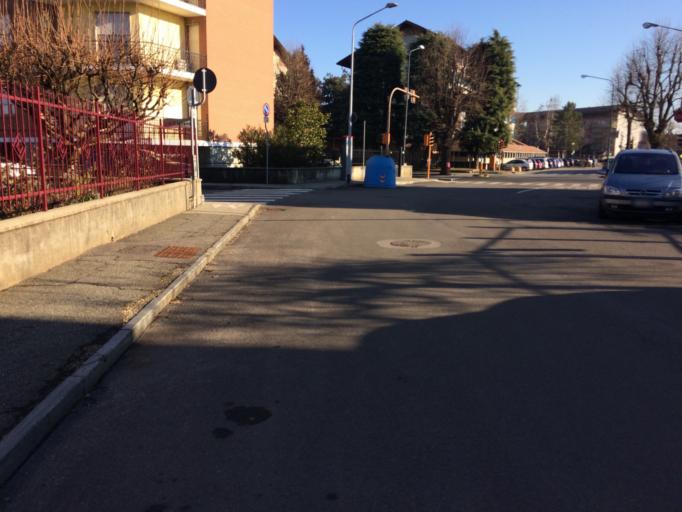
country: IT
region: Piedmont
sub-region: Provincia di Torino
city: Candiolo
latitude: 44.9608
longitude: 7.6033
